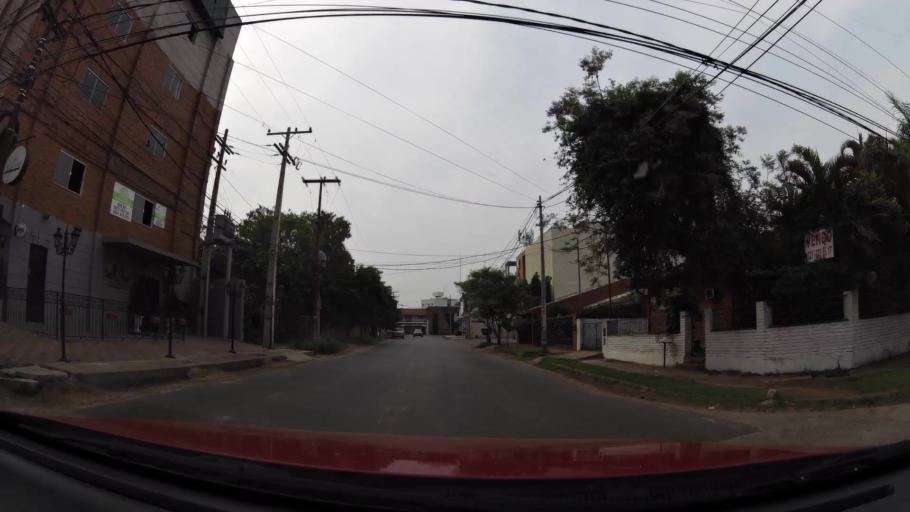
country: PY
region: Central
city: Fernando de la Mora
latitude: -25.2785
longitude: -57.5527
